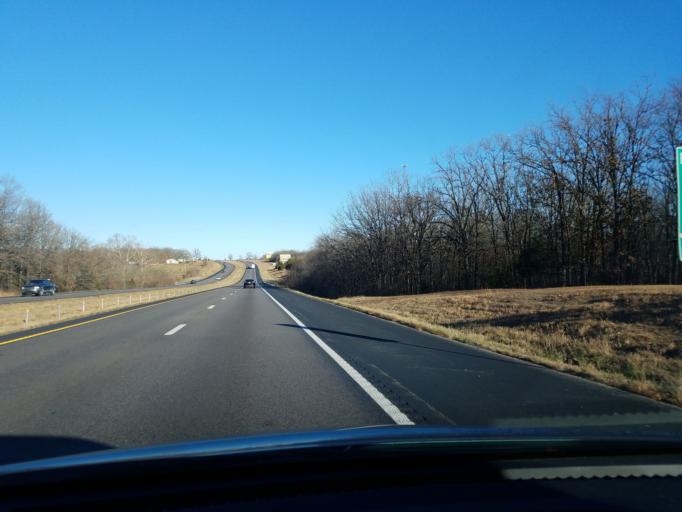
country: US
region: Missouri
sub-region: Phelps County
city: Saint James
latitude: 38.0134
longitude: -91.5914
